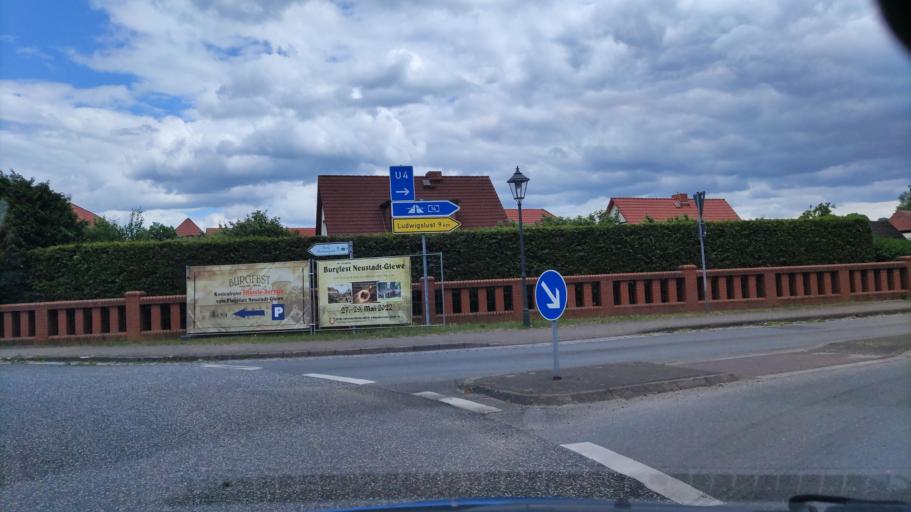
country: DE
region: Mecklenburg-Vorpommern
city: Neustadt-Glewe
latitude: 53.3836
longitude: 11.5817
